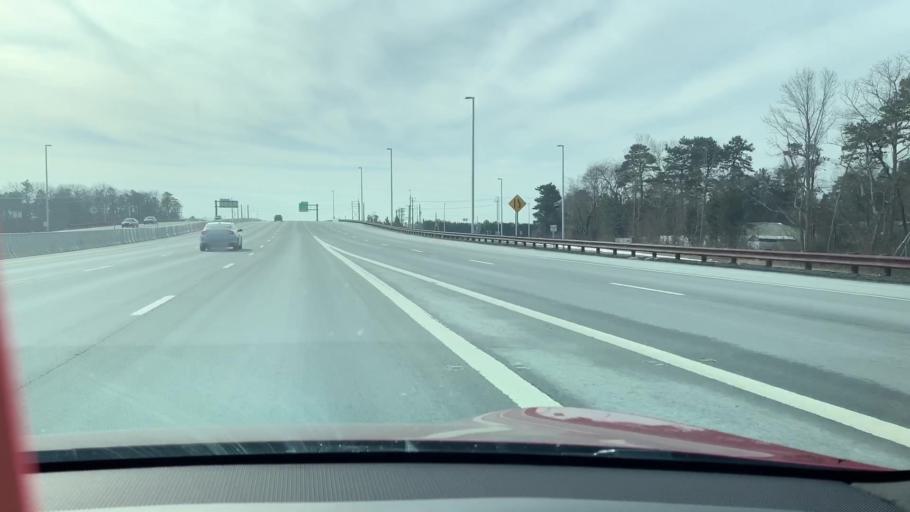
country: US
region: New Jersey
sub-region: Atlantic County
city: Pleasantville
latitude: 39.4071
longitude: -74.5566
